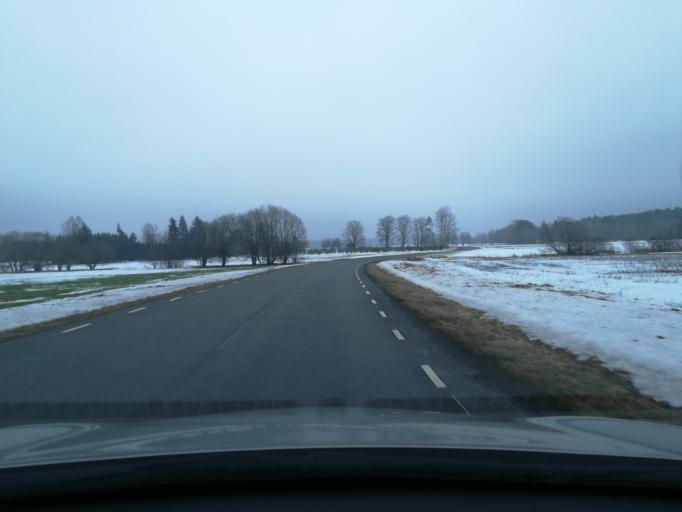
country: EE
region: Harju
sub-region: Kuusalu vald
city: Kuusalu
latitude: 59.4709
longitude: 25.5755
